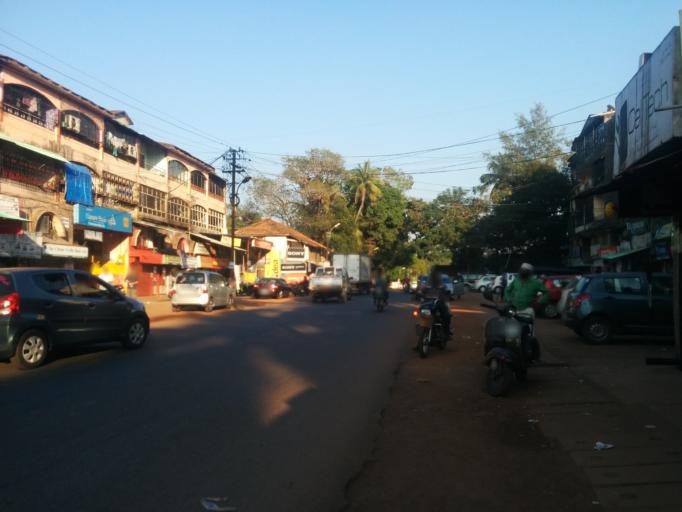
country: IN
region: Karnataka
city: Canacona
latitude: 15.0070
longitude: 74.0484
